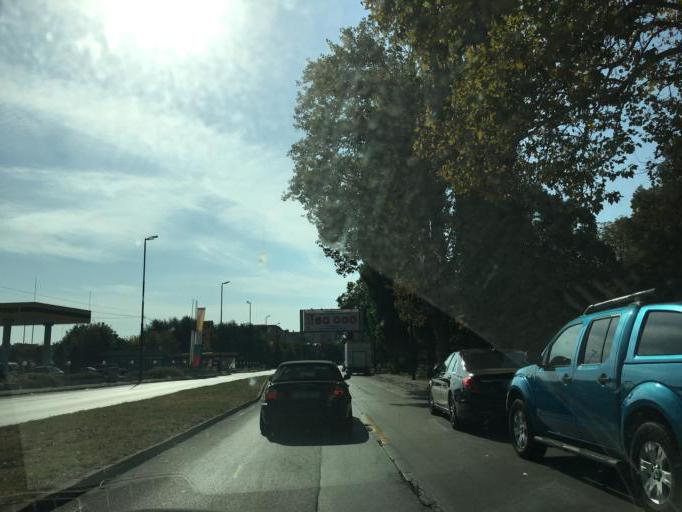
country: BG
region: Pazardzhik
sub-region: Obshtina Pazardzhik
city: Pazardzhik
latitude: 42.2083
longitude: 24.3268
